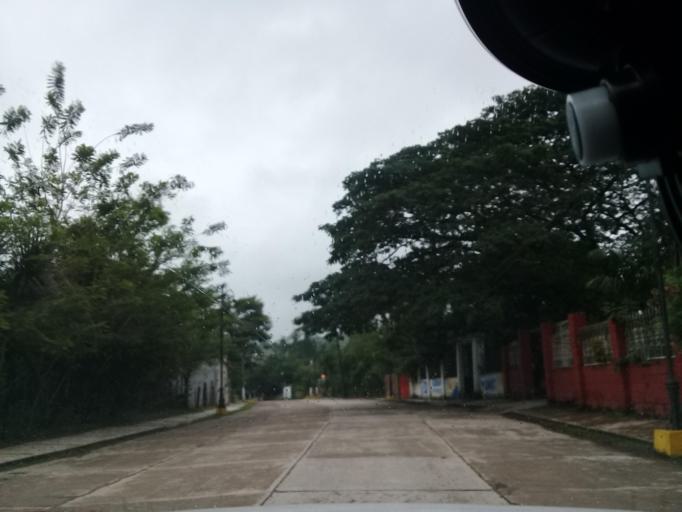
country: MX
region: Veracruz
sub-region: Chalma
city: San Pedro Coyutla
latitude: 21.2082
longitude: -98.3903
